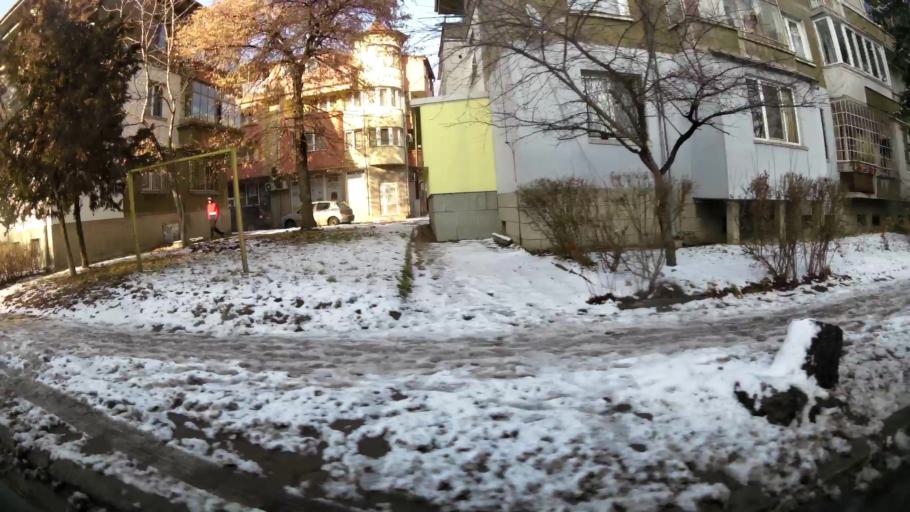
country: BG
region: Sofia-Capital
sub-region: Stolichna Obshtina
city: Sofia
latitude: 42.6687
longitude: 23.3591
